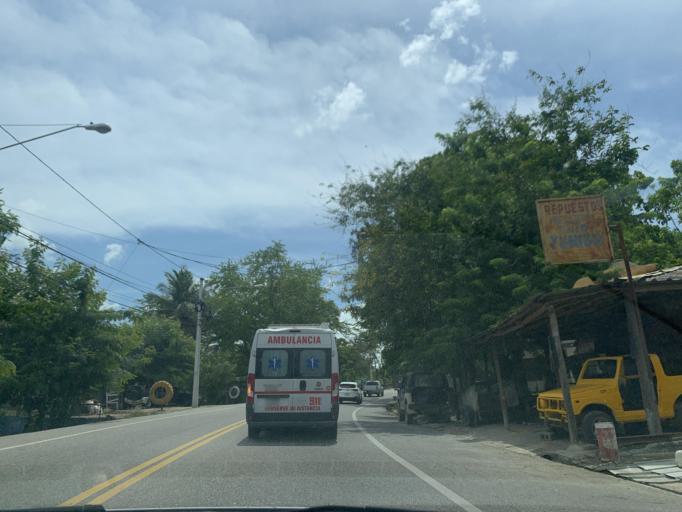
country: DO
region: Puerto Plata
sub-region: Puerto Plata
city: Puerto Plata
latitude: 19.7202
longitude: -70.6187
